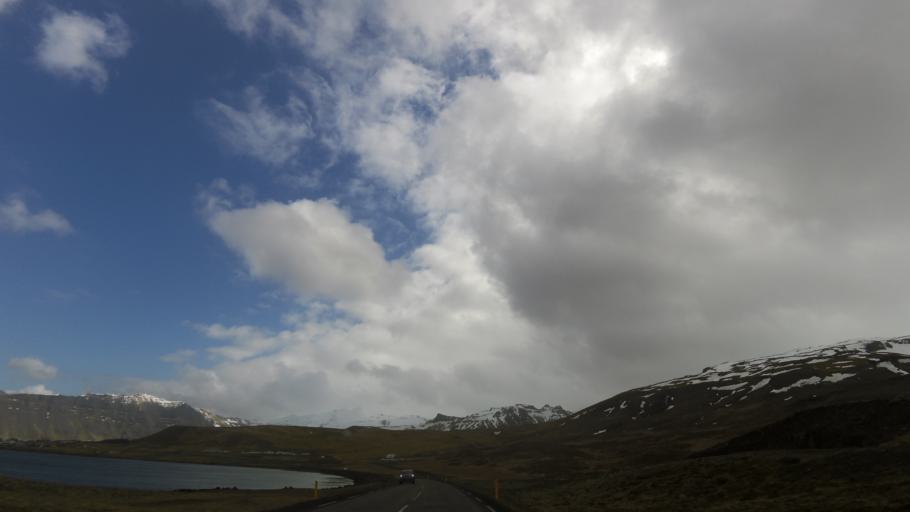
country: IS
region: West
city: Olafsvik
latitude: 64.9243
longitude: -23.2998
